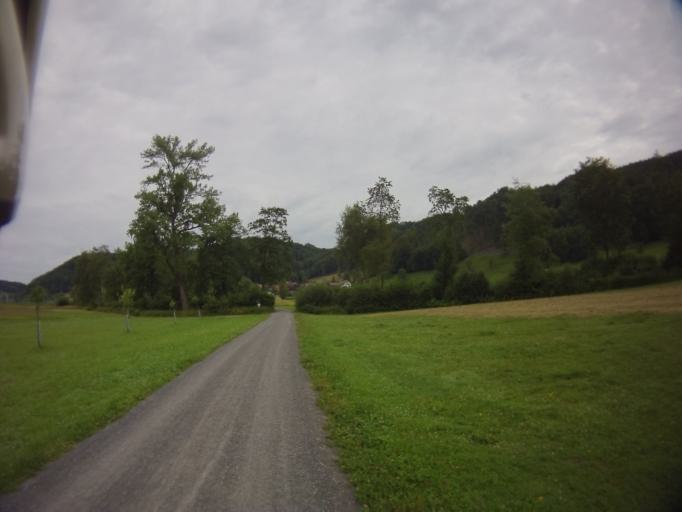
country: CH
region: Zurich
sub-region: Bezirk Affoltern
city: Hausen am Albis / Hausen (Dorf)
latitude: 47.2624
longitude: 8.5124
